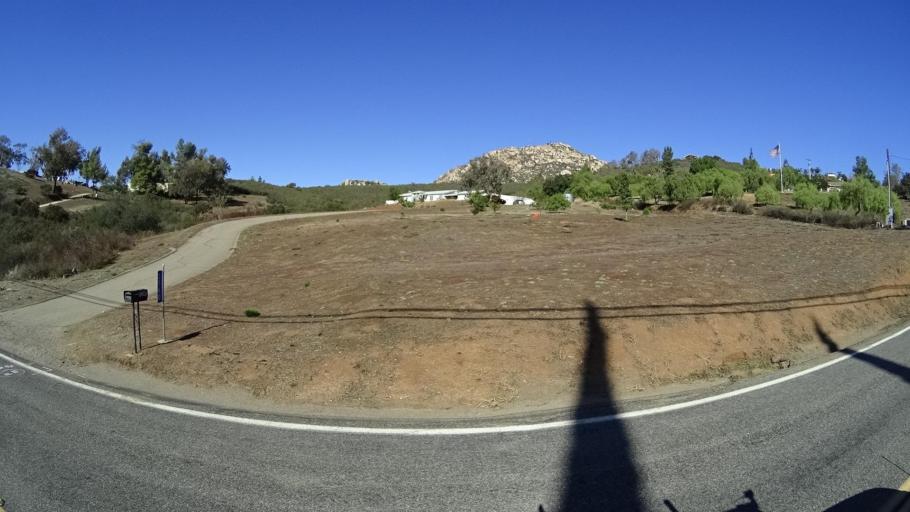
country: US
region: California
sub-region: San Diego County
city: Jamul
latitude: 32.6916
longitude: -116.7483
